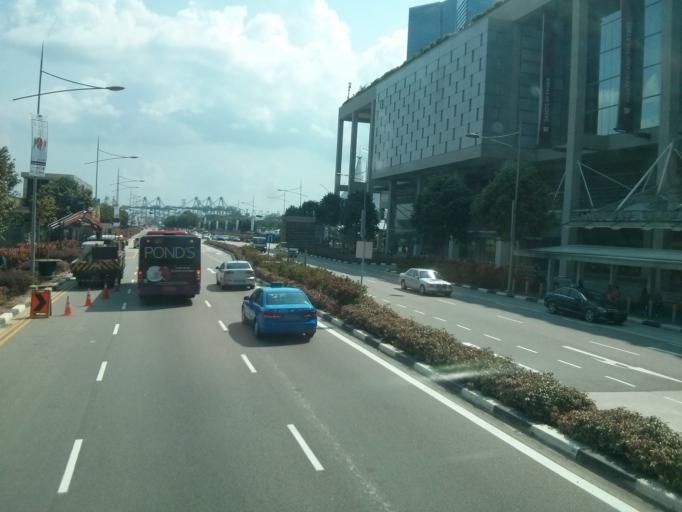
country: SG
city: Singapore
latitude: 1.2821
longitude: 103.8592
